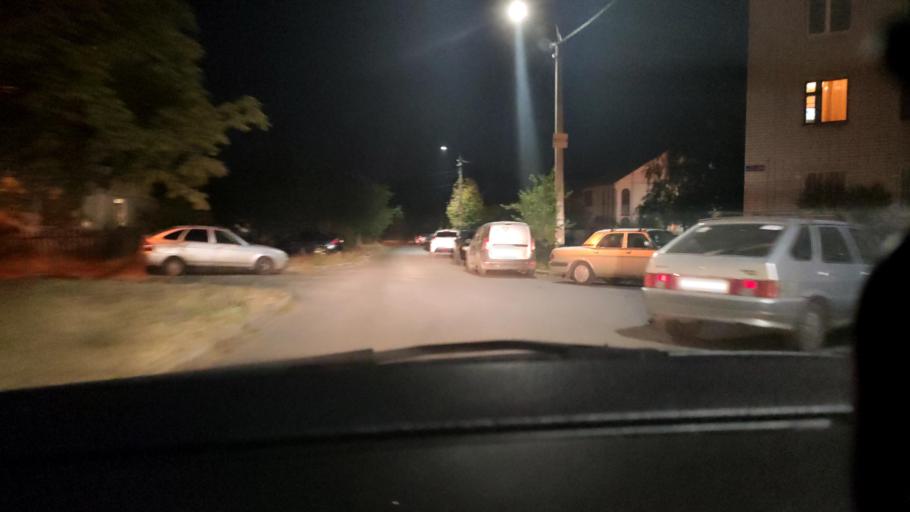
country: RU
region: Voronezj
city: Pridonskoy
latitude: 51.6609
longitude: 39.1189
